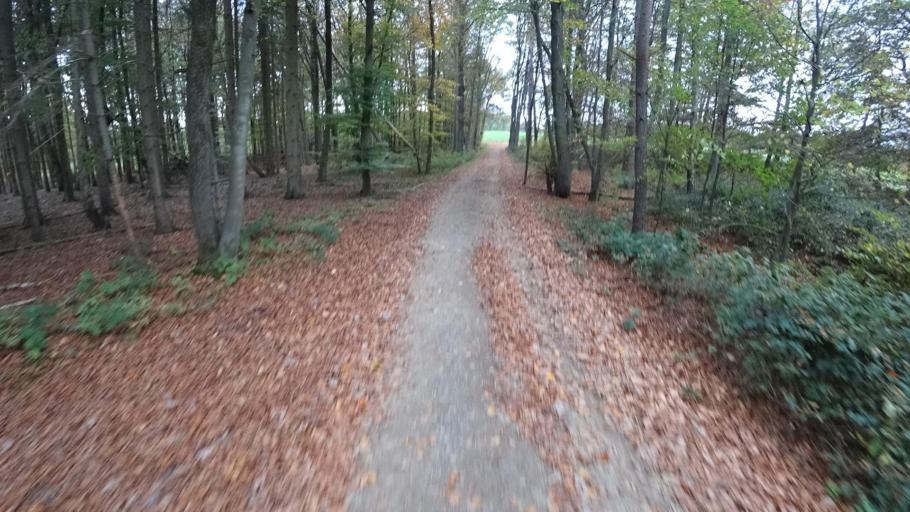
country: DE
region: Rheinland-Pfalz
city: Berg
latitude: 50.5571
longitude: 6.9327
